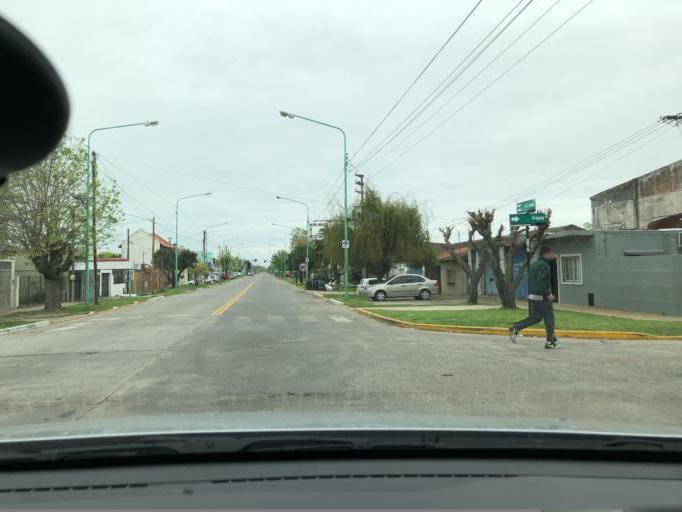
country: AR
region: Buenos Aires
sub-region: Partido de Ensenada
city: Ensenada
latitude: -34.8571
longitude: -57.9169
